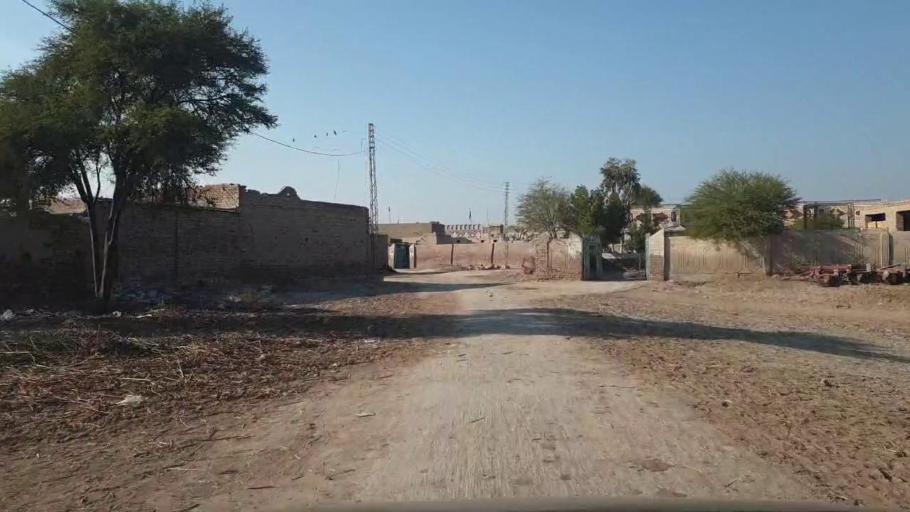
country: PK
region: Sindh
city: Shahpur Chakar
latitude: 26.1718
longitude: 68.6604
